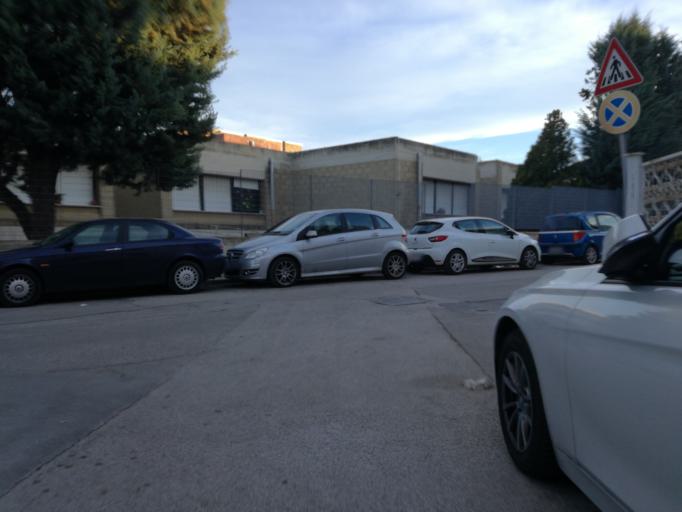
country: IT
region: Apulia
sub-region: Provincia di Bari
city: Valenzano
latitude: 41.0391
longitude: 16.8827
